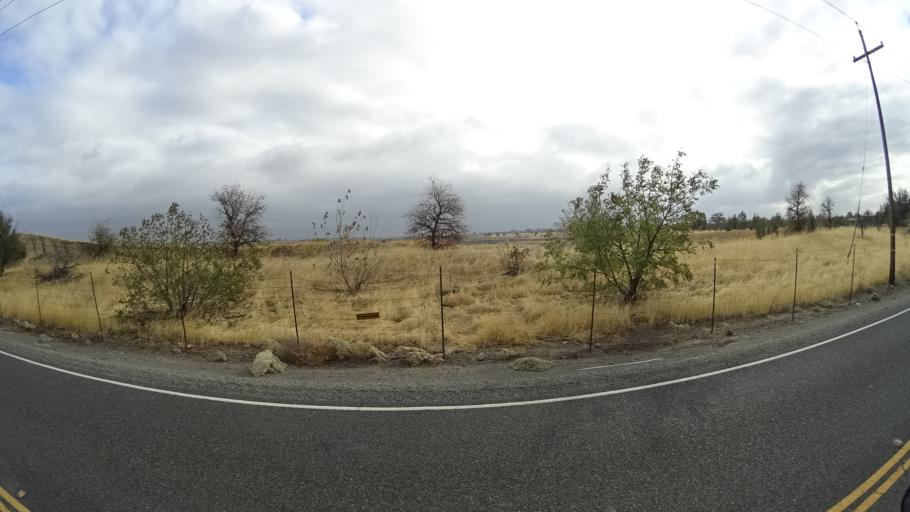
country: US
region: California
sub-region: Yolo County
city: Esparto
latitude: 38.7140
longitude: -122.0467
